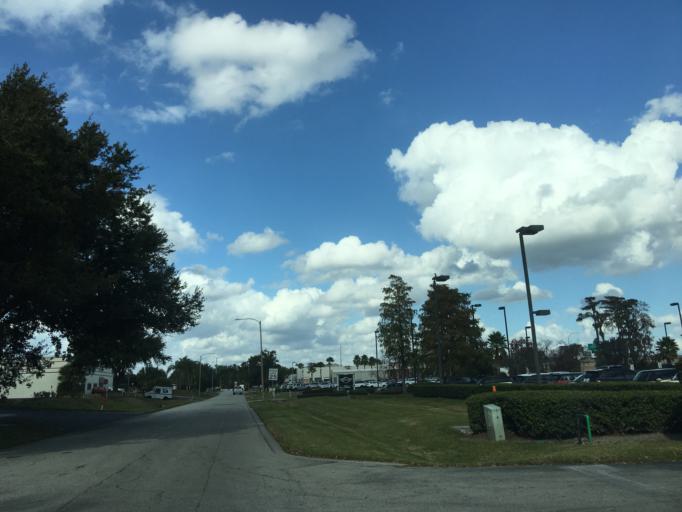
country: US
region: Florida
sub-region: Orange County
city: Eatonville
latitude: 28.6145
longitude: -81.3885
